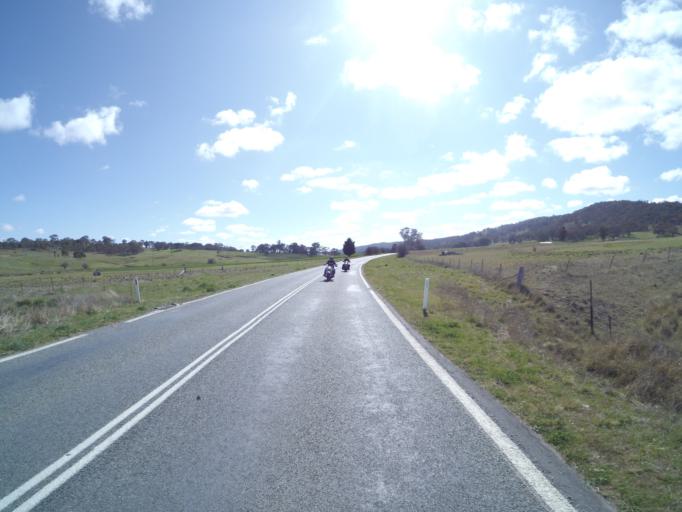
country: AU
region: New South Wales
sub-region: Queanbeyan
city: Queanbeyan
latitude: -35.3153
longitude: 149.2445
